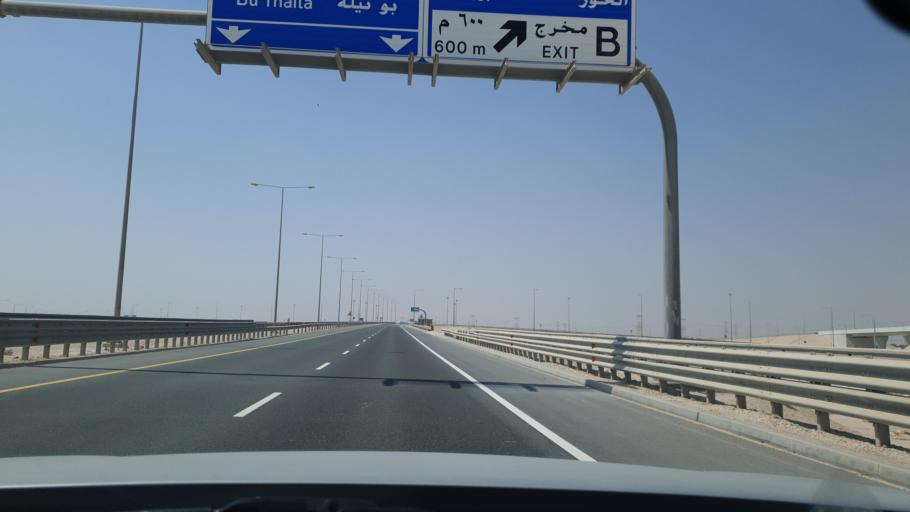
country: QA
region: Baladiyat az Za`ayin
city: Az Za`ayin
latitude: 25.6177
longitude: 51.3741
